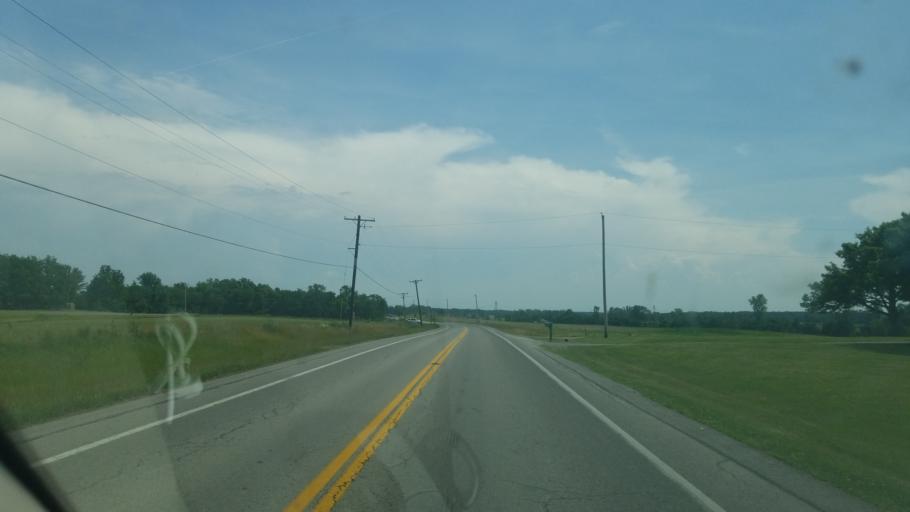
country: US
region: Ohio
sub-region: Logan County
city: Northwood
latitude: 40.4655
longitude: -83.7312
